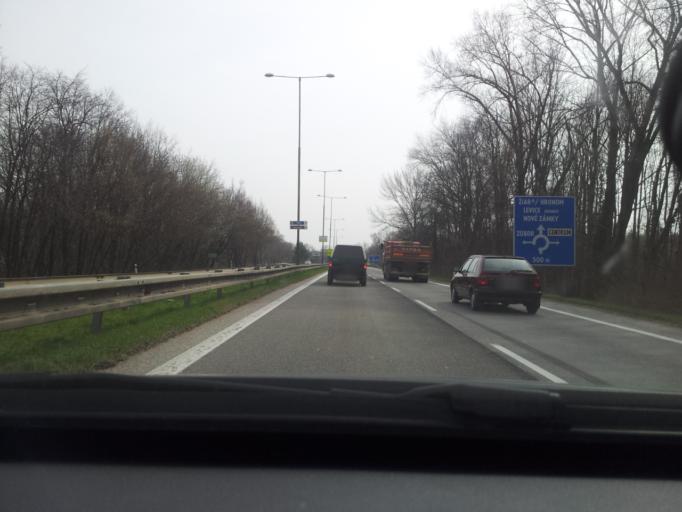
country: SK
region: Nitriansky
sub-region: Okres Nitra
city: Nitra
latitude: 48.3219
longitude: 18.0919
